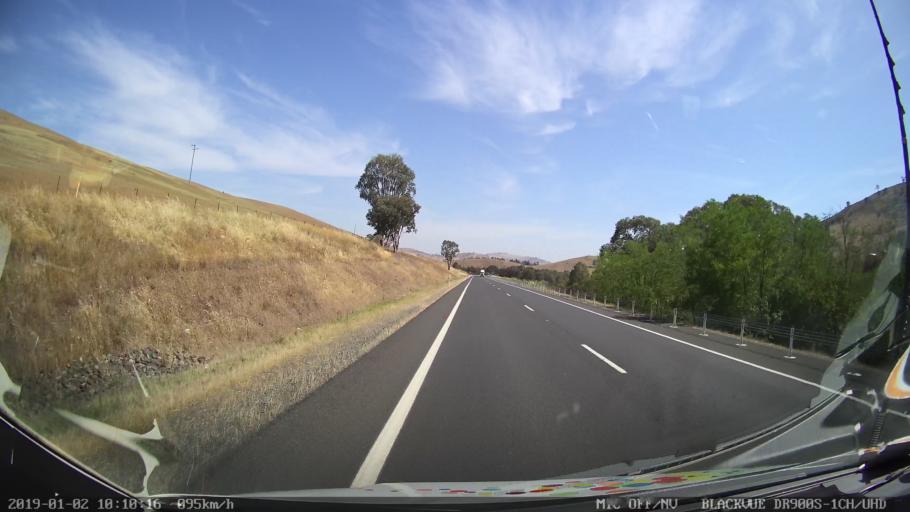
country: AU
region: New South Wales
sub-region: Gundagai
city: Gundagai
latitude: -35.1062
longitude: 148.0967
